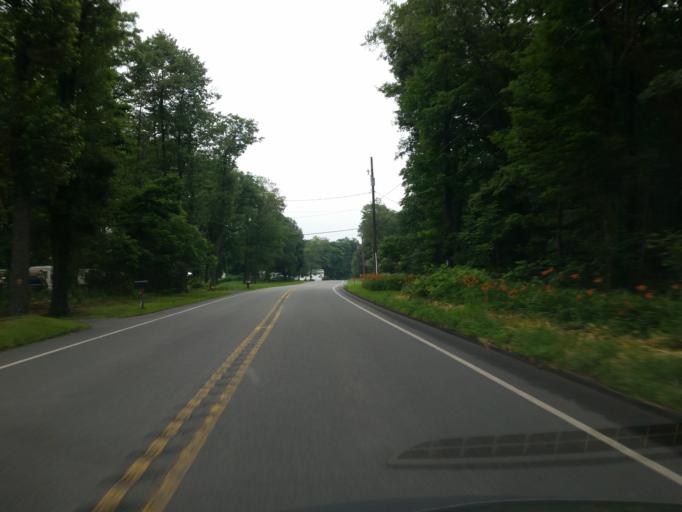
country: US
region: Pennsylvania
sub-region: Schuylkill County
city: Valley View
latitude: 40.6110
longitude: -76.4683
